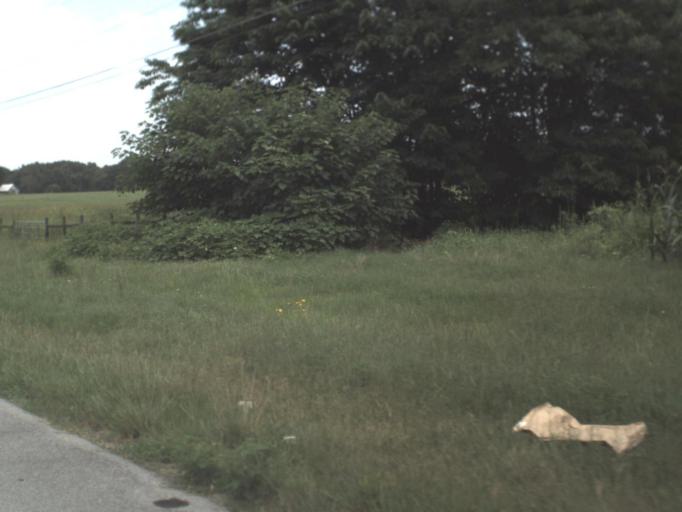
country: US
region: Florida
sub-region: Madison County
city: Madison
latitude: 30.4796
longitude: -83.4166
